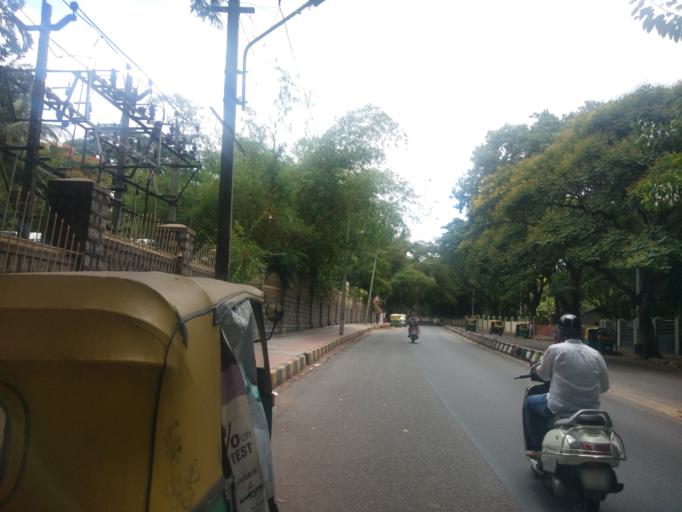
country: IN
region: Karnataka
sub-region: Bangalore Urban
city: Bangalore
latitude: 12.9952
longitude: 77.5986
